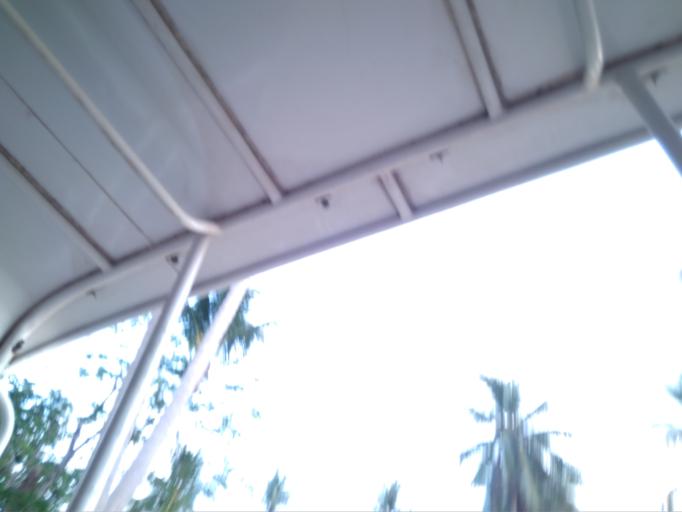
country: TH
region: Phangnga
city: Ko Yao
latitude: 8.1664
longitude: 98.6146
